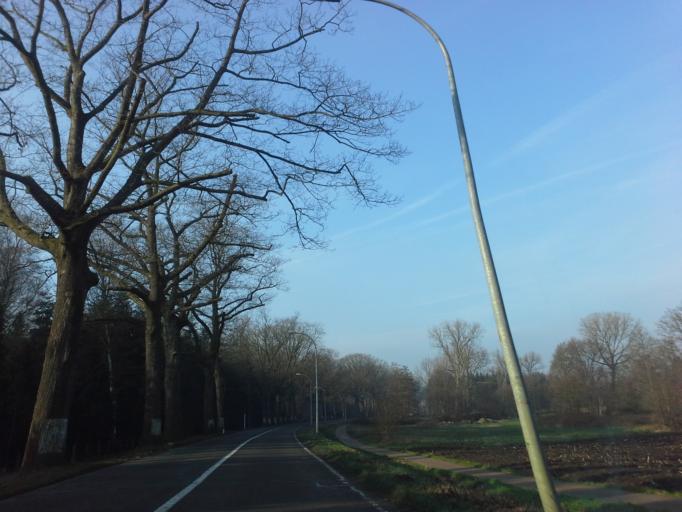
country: BE
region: Flanders
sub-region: Provincie Antwerpen
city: Meerhout
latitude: 51.1434
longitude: 5.0528
